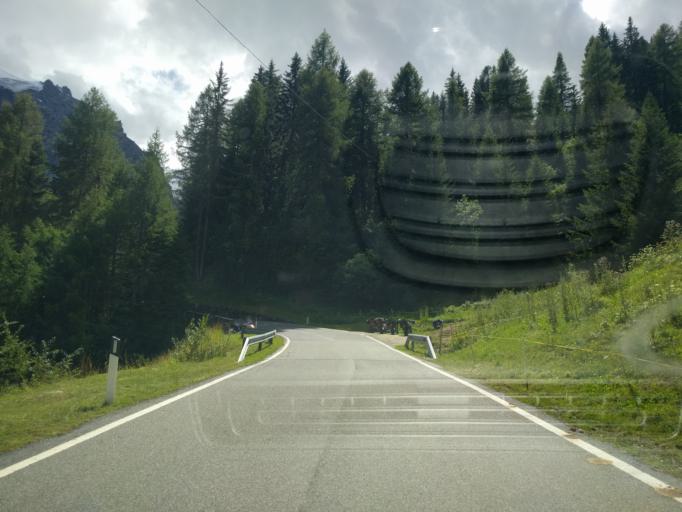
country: IT
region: Trentino-Alto Adige
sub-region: Bolzano
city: Stelvio
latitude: 46.5422
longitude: 10.5031
